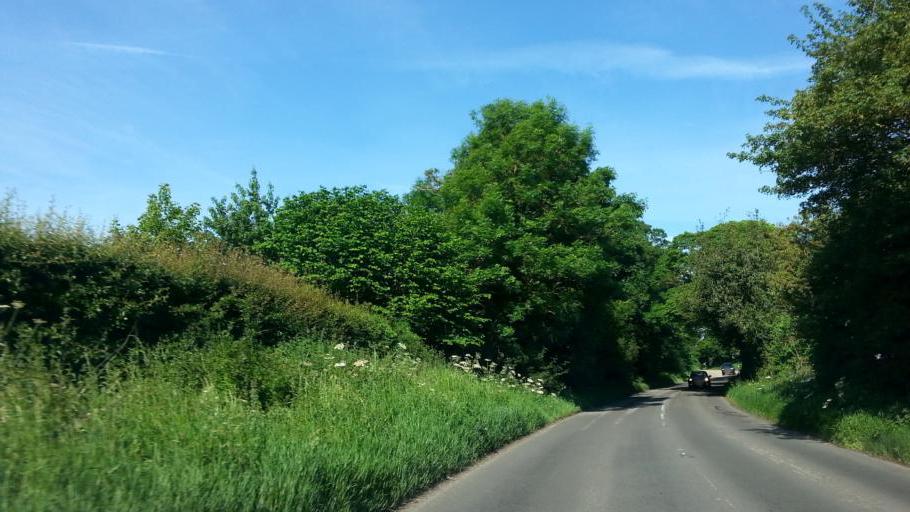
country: GB
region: England
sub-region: Nottinghamshire
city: Southwell
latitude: 53.0760
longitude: -0.9863
